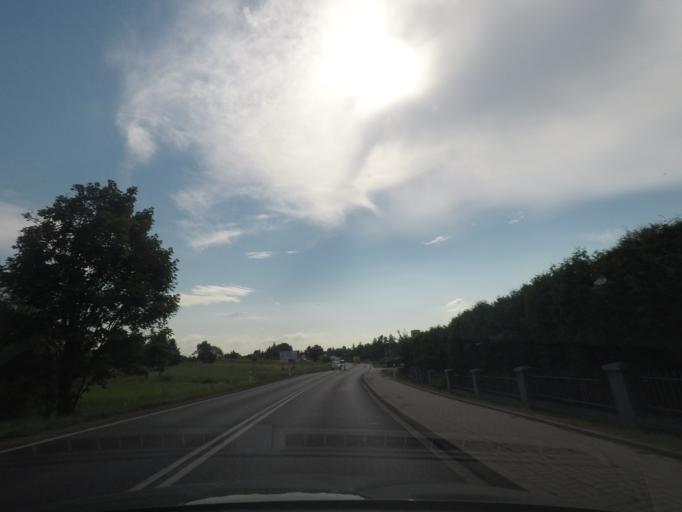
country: PL
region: Lesser Poland Voivodeship
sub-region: Powiat oswiecimski
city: Brzeszcze
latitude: 49.9783
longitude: 19.1493
